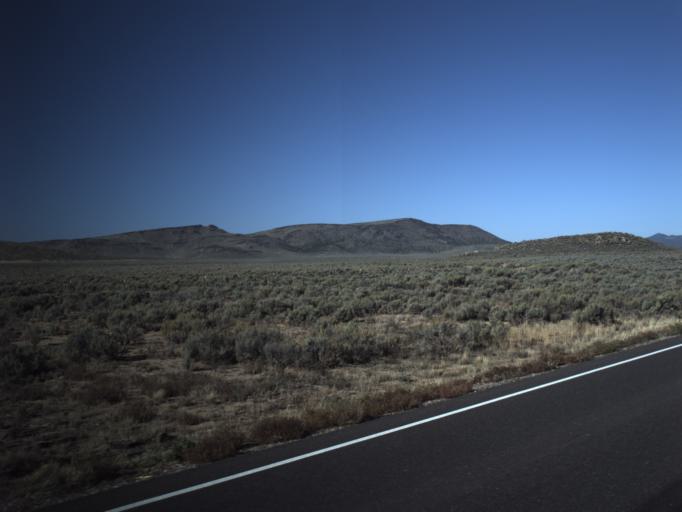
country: US
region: Utah
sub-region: Washington County
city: Enterprise
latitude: 37.7747
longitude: -113.8416
